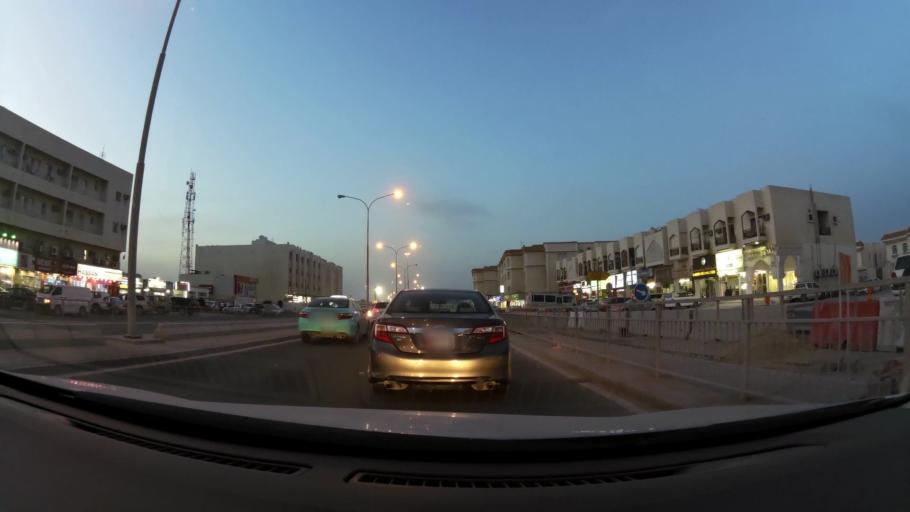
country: QA
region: Al Wakrah
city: Al Wakrah
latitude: 25.1702
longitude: 51.5978
